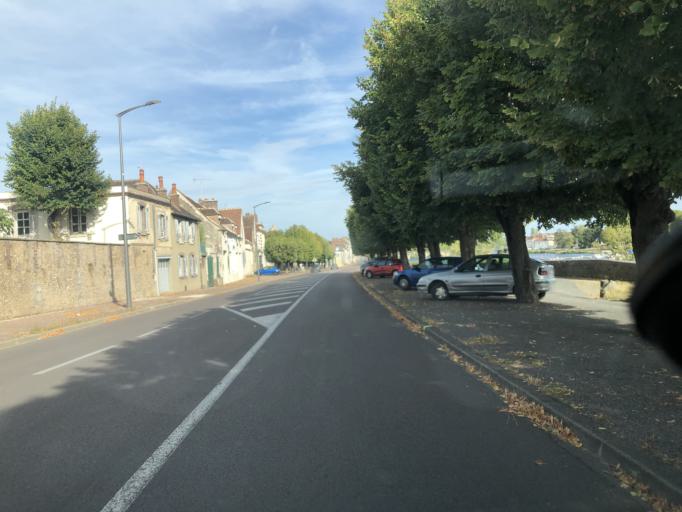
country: FR
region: Bourgogne
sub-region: Departement de l'Yonne
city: Joigny
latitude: 47.9832
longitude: 3.3878
